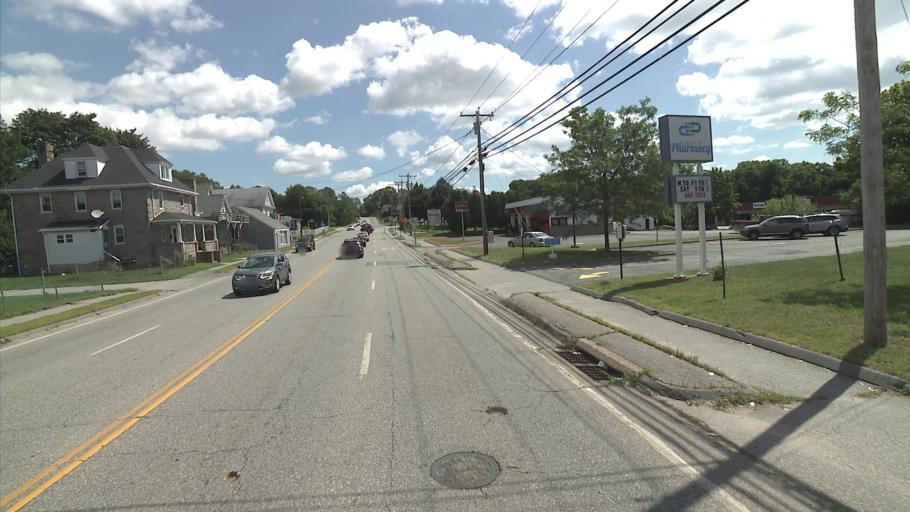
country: US
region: Connecticut
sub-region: New London County
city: Central Waterford
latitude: 41.3417
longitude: -72.1220
